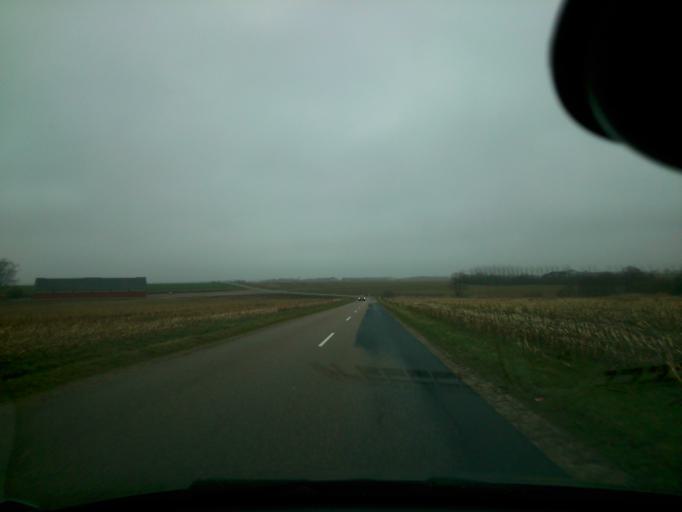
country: DK
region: Central Jutland
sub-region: Ringkobing-Skjern Kommune
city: Ringkobing
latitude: 56.0908
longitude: 8.4014
